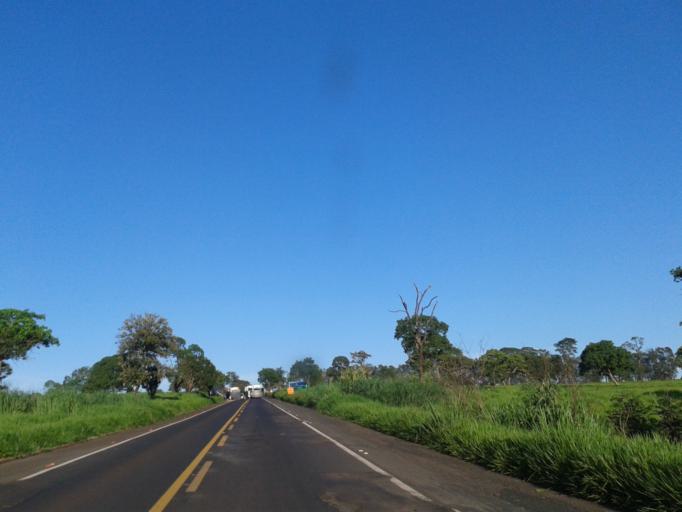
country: BR
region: Minas Gerais
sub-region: Santa Vitoria
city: Santa Vitoria
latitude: -18.9387
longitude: -49.8178
